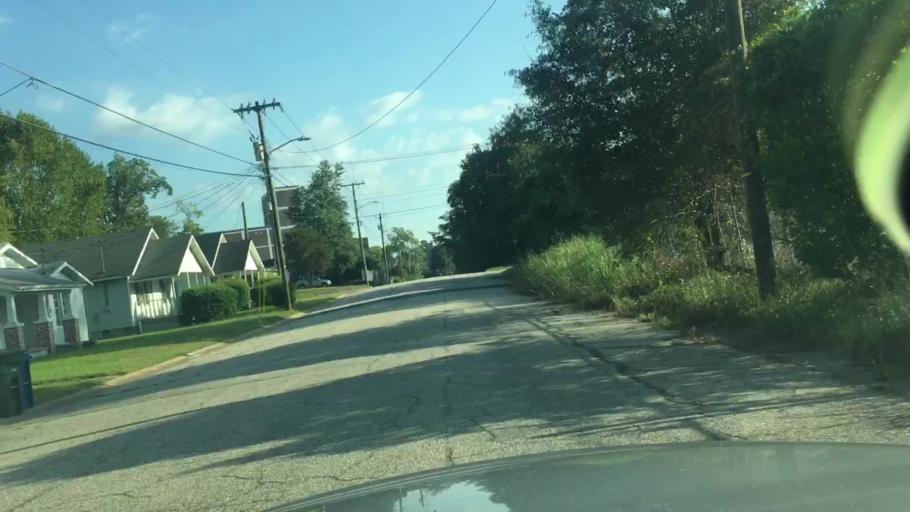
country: US
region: North Carolina
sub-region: Cumberland County
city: Fayetteville
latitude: 35.0504
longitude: -78.8905
